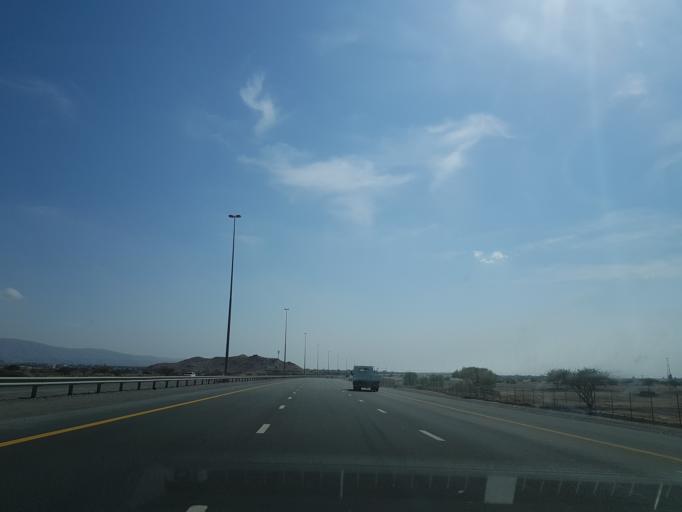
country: AE
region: Ra's al Khaymah
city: Ras al-Khaimah
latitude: 25.7371
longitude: 56.0149
